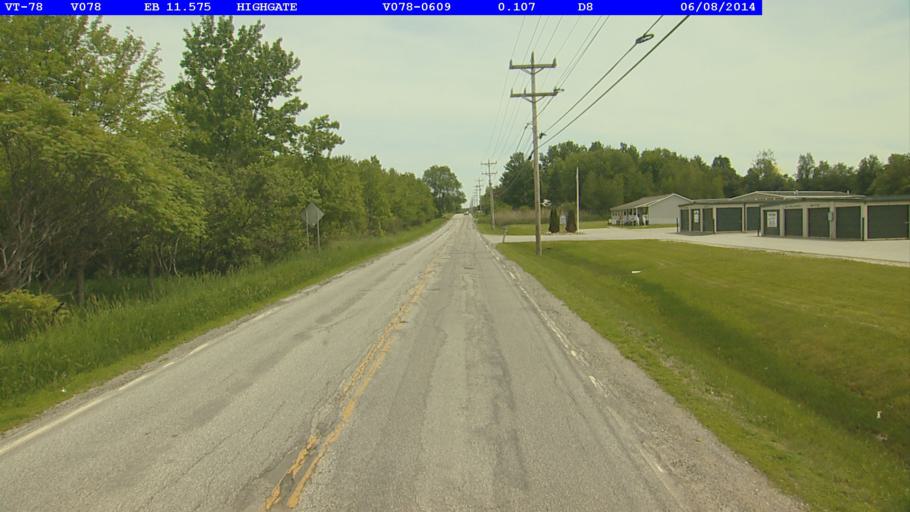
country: US
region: Vermont
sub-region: Franklin County
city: Swanton
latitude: 44.9267
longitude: -73.0965
